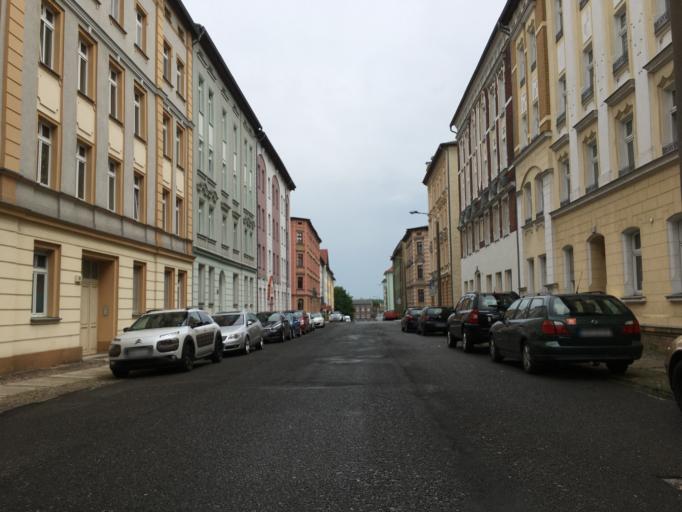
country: DE
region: Brandenburg
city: Eberswalde
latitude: 52.8349
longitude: 13.8040
